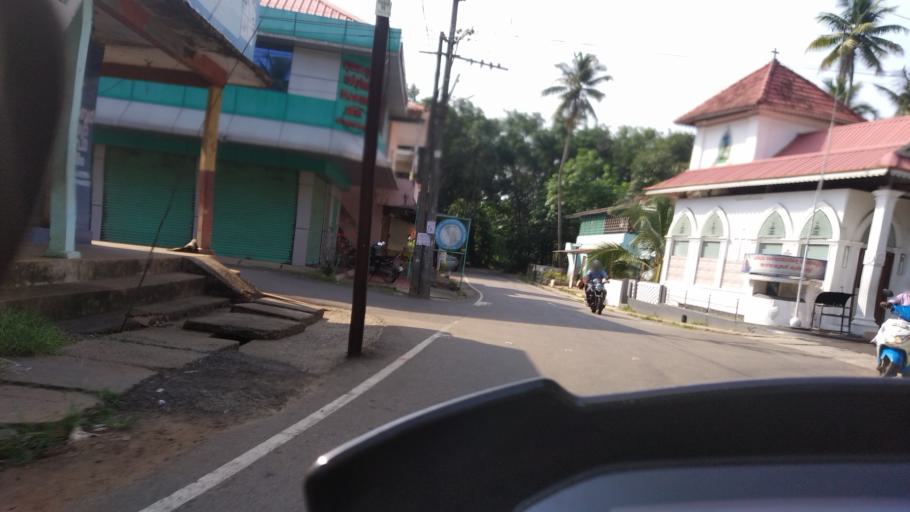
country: IN
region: Kerala
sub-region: Ernakulam
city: Piravam
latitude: 9.8525
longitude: 76.5309
